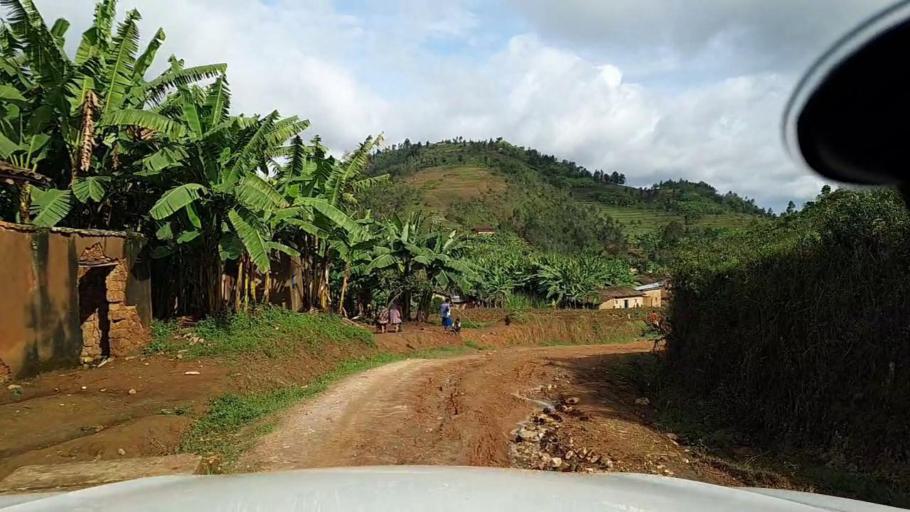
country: RW
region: Western Province
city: Kibuye
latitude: -2.1341
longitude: 29.5035
